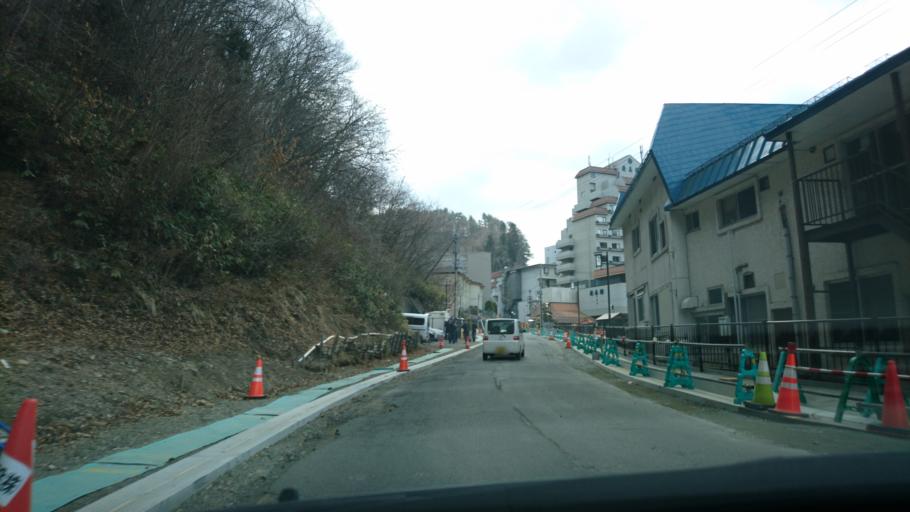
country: JP
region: Iwate
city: Shizukuishi
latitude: 39.6743
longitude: 141.0215
